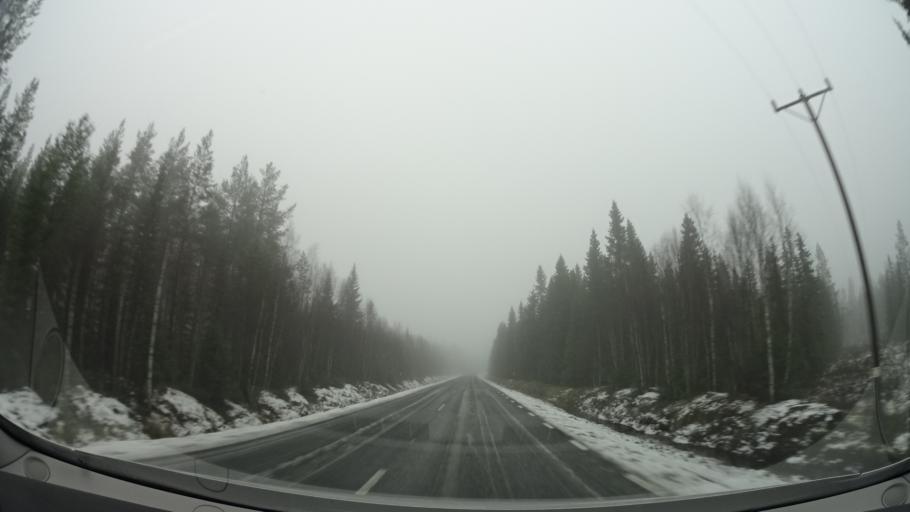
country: SE
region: Vaesterbotten
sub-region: Asele Kommun
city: Insjon
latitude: 64.2675
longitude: 17.5717
